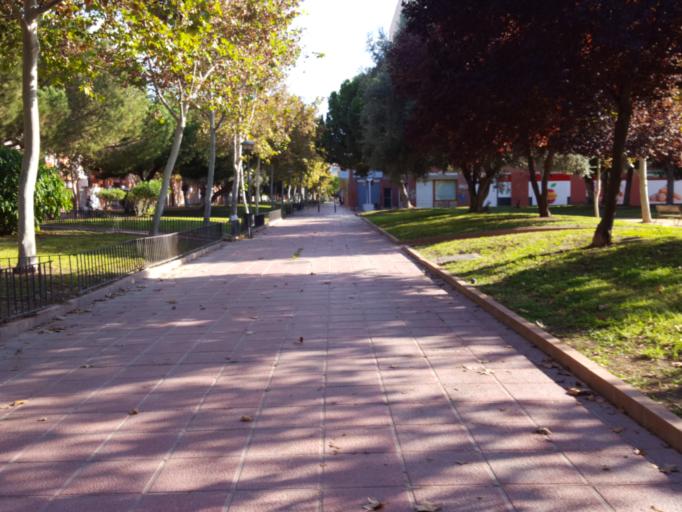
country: ES
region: Murcia
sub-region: Murcia
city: Murcia
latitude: 37.9960
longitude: -1.1247
